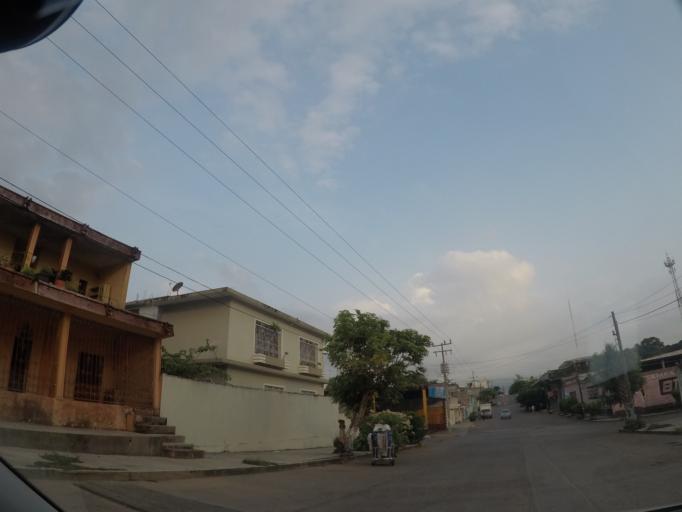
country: MX
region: Oaxaca
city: Matias Romero
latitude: 16.8748
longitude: -95.0391
